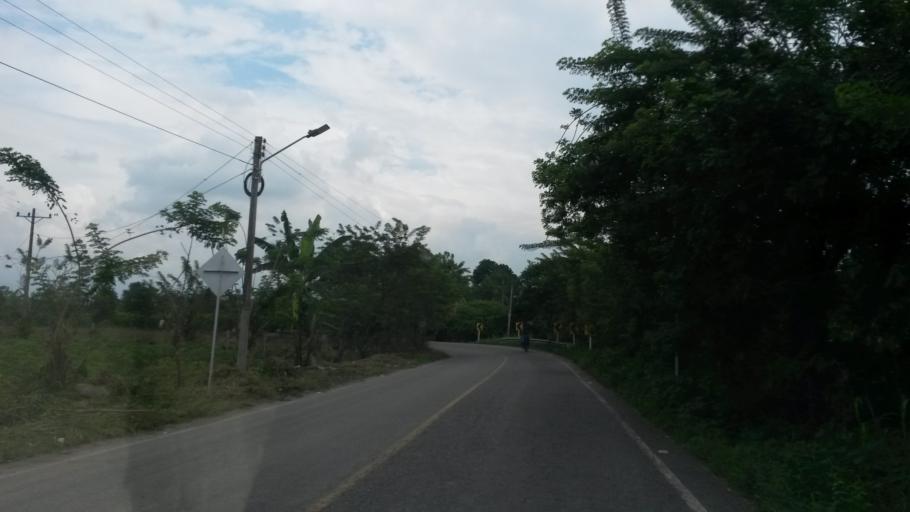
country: CO
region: Cauca
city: Padilla
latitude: 3.2304
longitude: -76.3277
